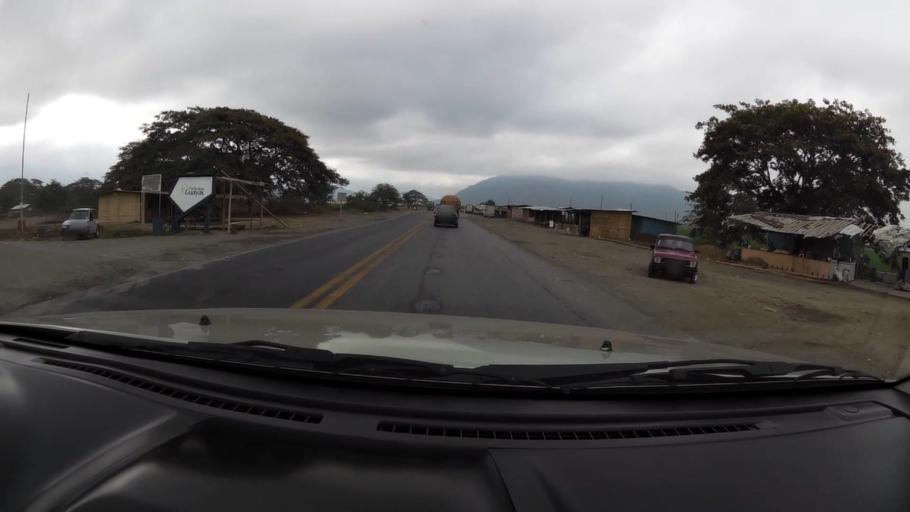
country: EC
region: Guayas
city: Coronel Marcelino Mariduena
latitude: -2.3507
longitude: -79.6341
